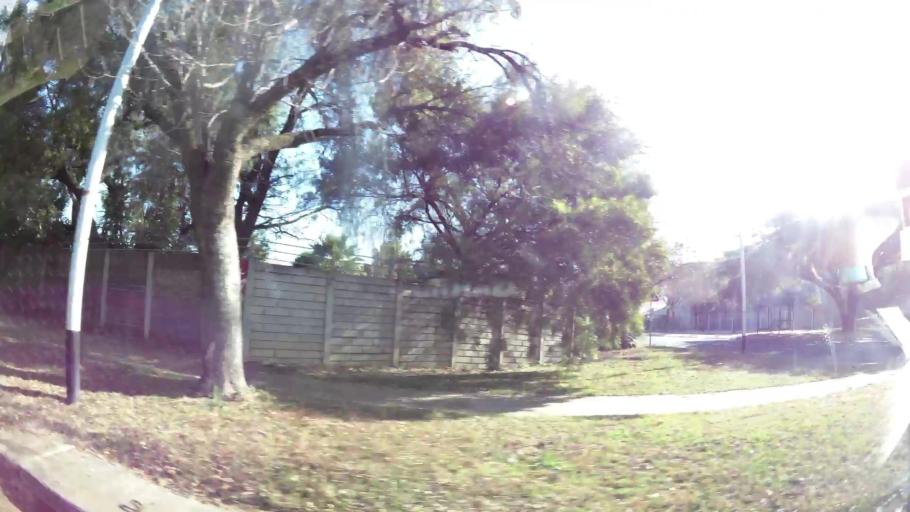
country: ZA
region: Gauteng
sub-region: City of Tshwane Metropolitan Municipality
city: Pretoria
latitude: -25.7251
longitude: 28.2478
